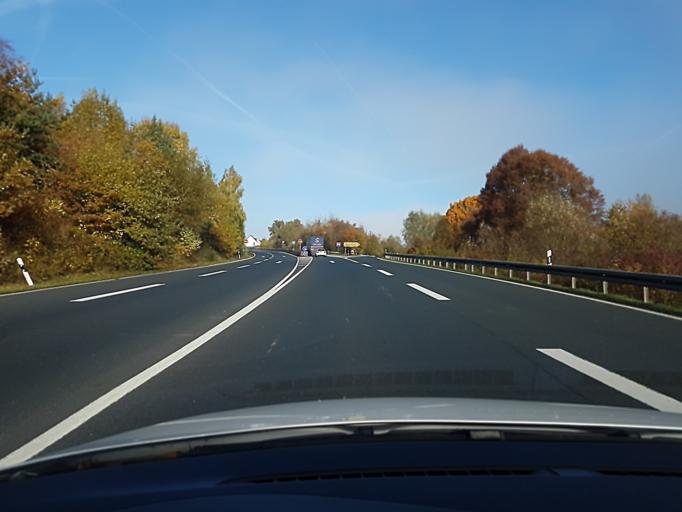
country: DE
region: Bavaria
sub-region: Regierungsbezirk Unterfranken
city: Klingenberg am Main
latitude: 49.7672
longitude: 9.1771
